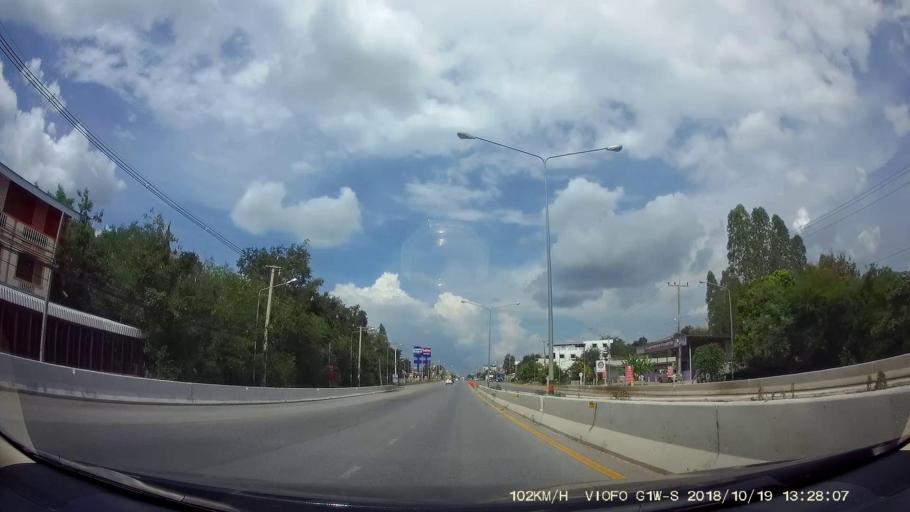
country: TH
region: Chaiyaphum
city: Chatturat
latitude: 15.5573
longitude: 101.8460
